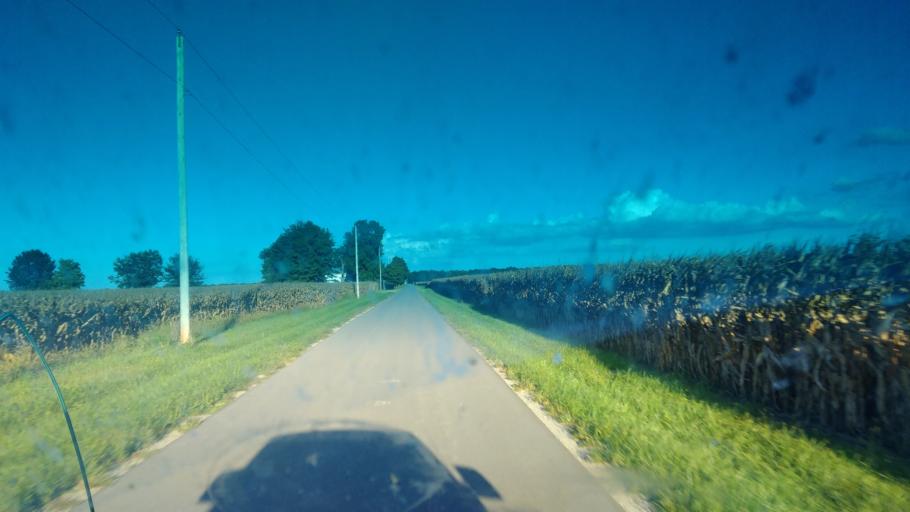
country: US
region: Ohio
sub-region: Wyandot County
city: Upper Sandusky
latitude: 40.8910
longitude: -83.2681
